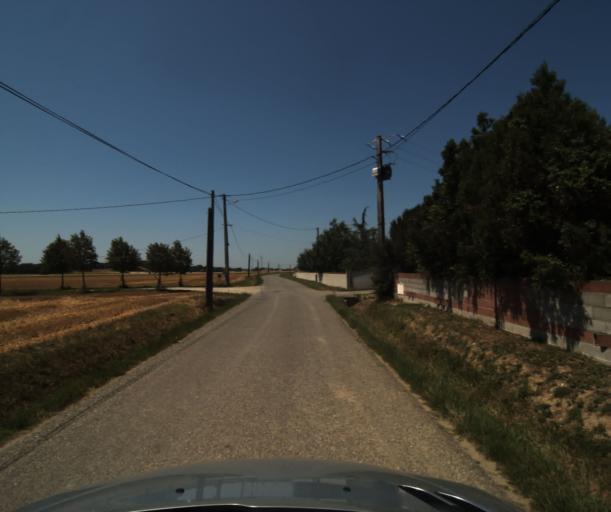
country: FR
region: Midi-Pyrenees
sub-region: Departement de la Haute-Garonne
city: Muret
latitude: 43.4687
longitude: 1.3641
